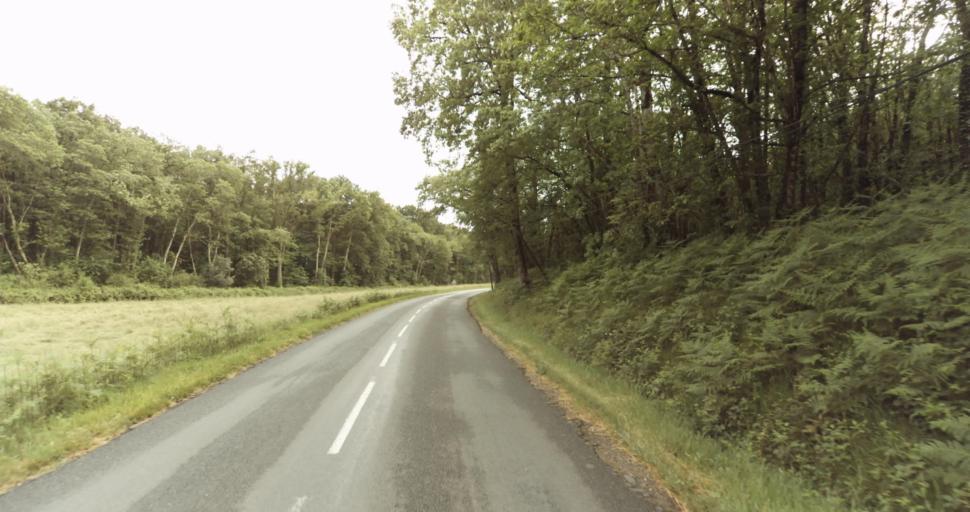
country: FR
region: Aquitaine
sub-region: Departement de la Dordogne
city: Belves
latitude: 44.7085
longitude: 0.9336
